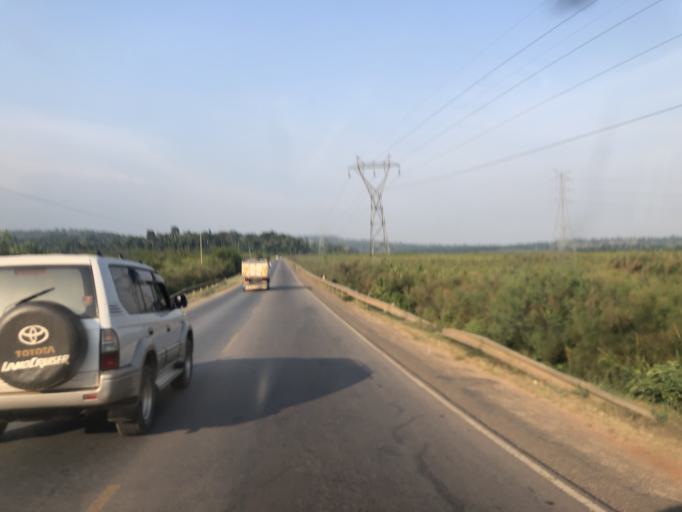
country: UG
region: Central Region
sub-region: Butambala District
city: Gombe
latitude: 0.1225
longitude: 32.1925
